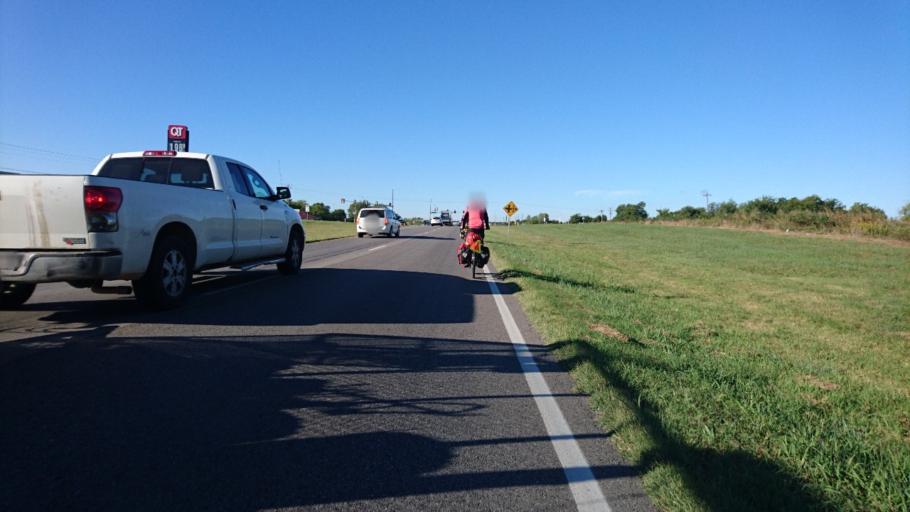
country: US
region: Oklahoma
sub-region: Rogers County
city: Verdigris
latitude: 36.2510
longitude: -95.6673
